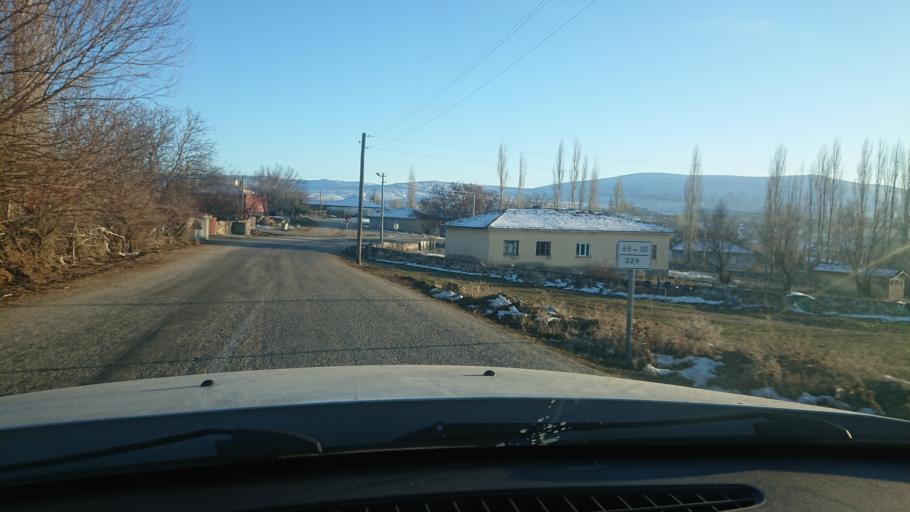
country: TR
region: Aksaray
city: Ortakoy
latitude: 38.7572
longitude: 33.9339
